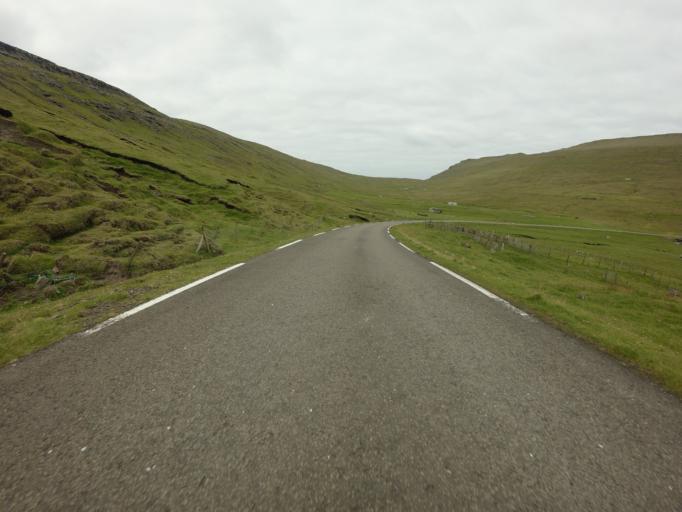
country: FO
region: Suduroy
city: Tvoroyri
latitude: 61.6252
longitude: -6.9418
